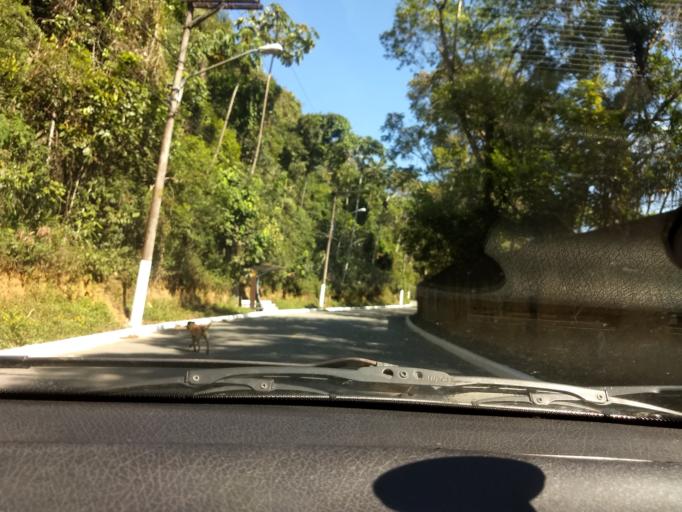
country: BR
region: Sao Paulo
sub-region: Embu-Guacu
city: Embu Guacu
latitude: -23.8061
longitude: -46.7425
